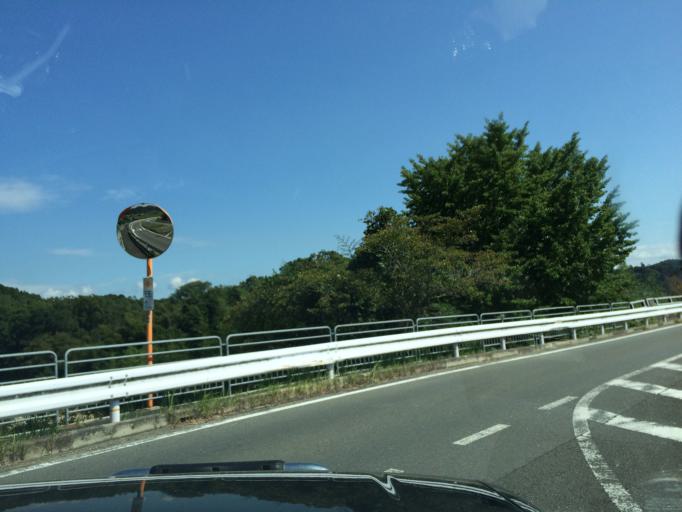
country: JP
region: Kyoto
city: Kameoka
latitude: 35.1098
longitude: 135.4567
